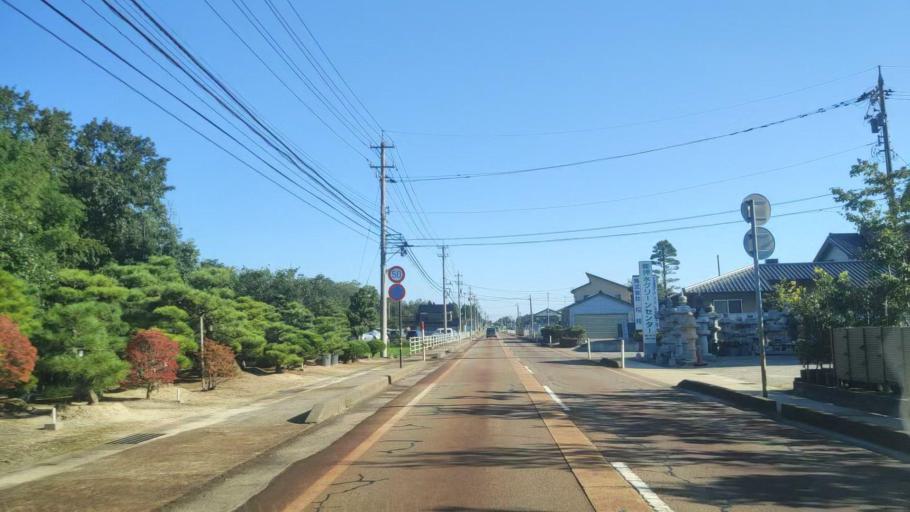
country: JP
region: Ishikawa
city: Hakui
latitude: 36.8109
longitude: 136.7548
